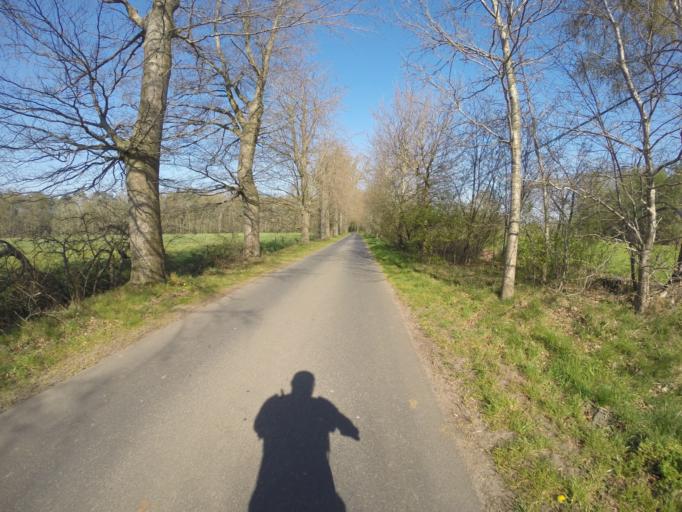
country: BE
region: Flanders
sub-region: Provincie West-Vlaanderen
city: Beernem
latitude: 51.1016
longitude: 3.3678
